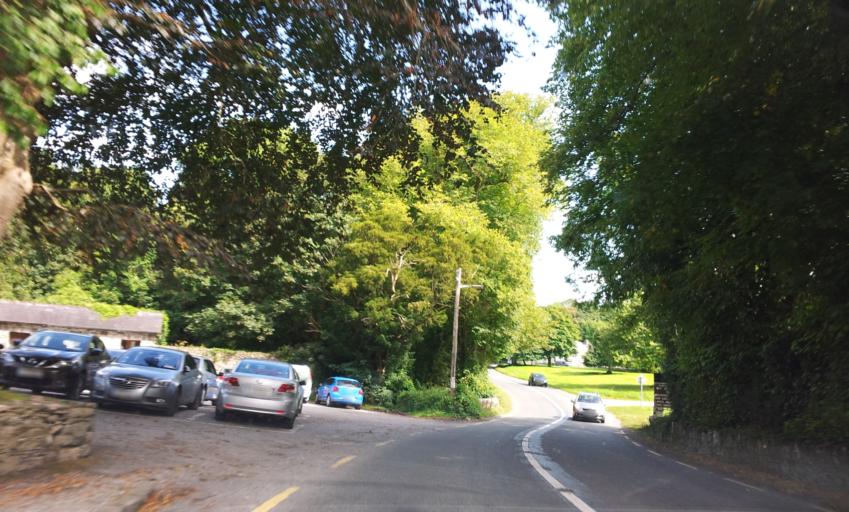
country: IE
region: Munster
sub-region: Ciarrai
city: Cill Airne
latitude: 52.0254
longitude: -9.4898
